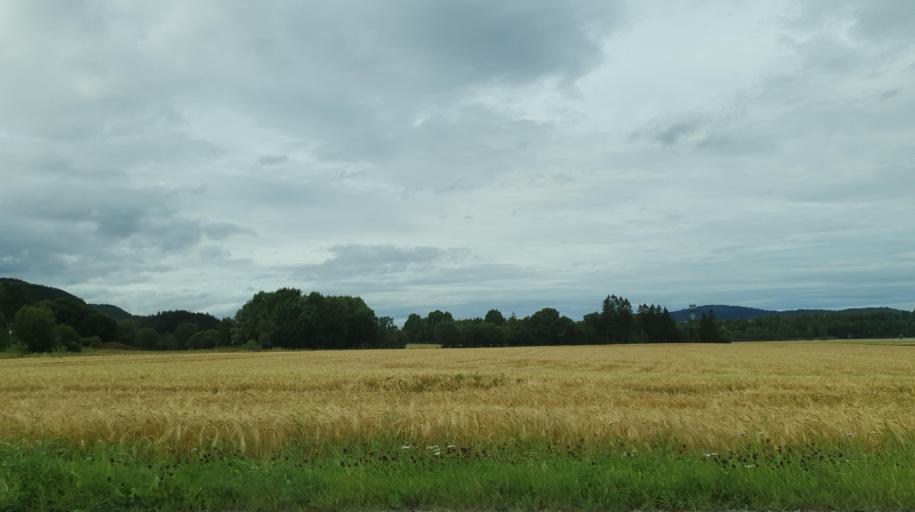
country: NO
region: Nord-Trondelag
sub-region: Stjordal
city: Stjordalshalsen
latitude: 63.4457
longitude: 10.9413
